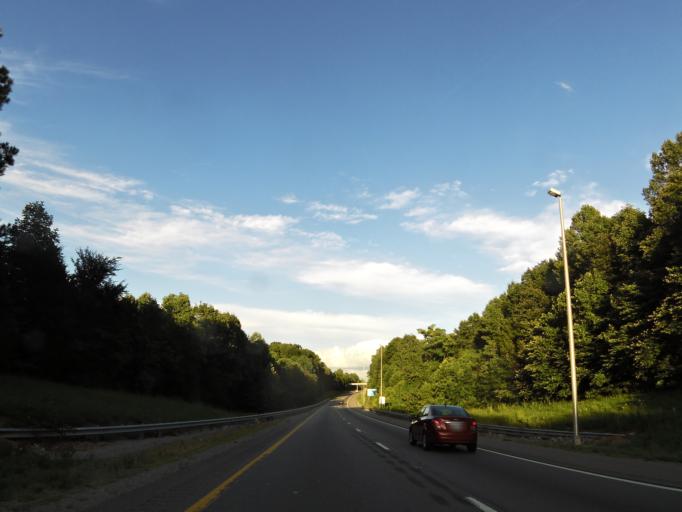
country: US
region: Tennessee
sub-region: Putnam County
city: Cookeville
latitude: 36.1372
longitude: -85.4942
